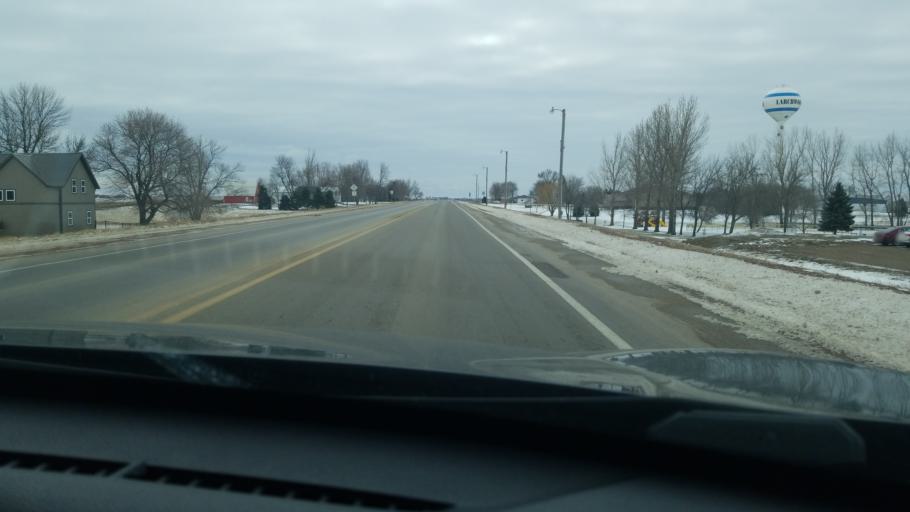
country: US
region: South Dakota
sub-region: Minnehaha County
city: Brandon
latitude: 43.4516
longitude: -96.4297
